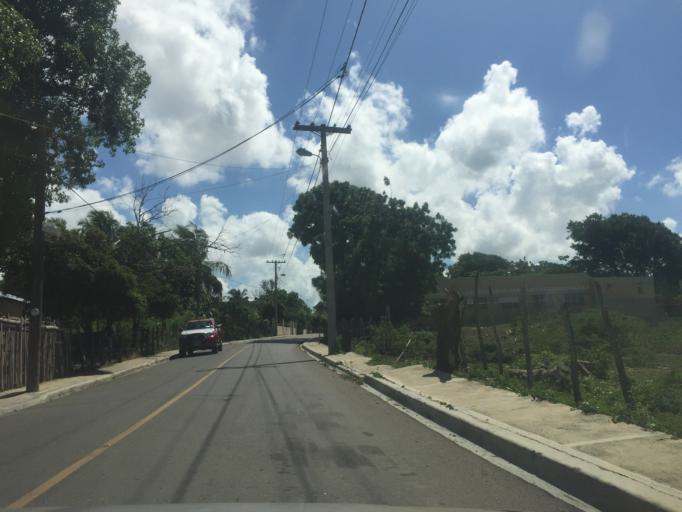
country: DO
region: Santiago
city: Santiago de los Caballeros
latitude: 19.4469
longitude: -70.7560
